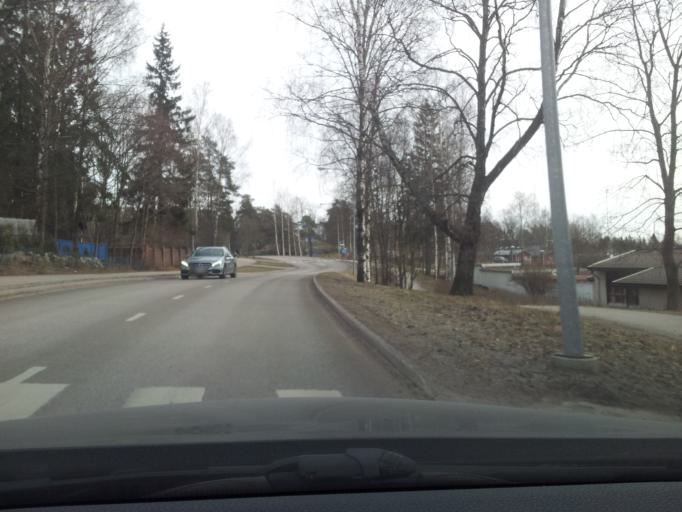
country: FI
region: Uusimaa
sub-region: Helsinki
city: Kilo
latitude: 60.1924
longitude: 24.7654
